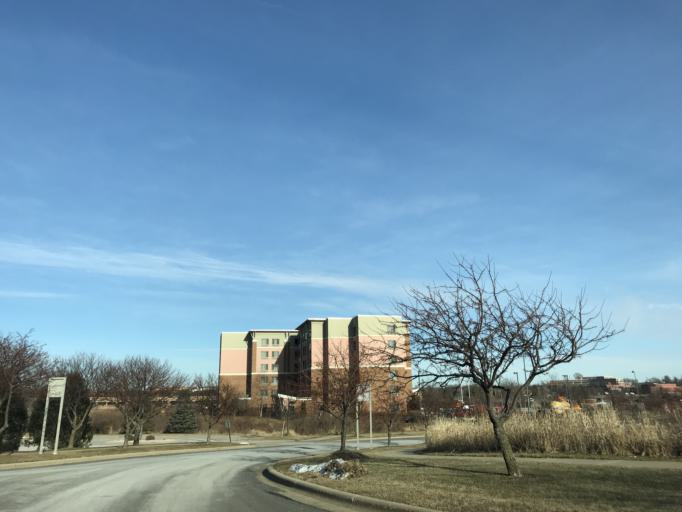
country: US
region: Wisconsin
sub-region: Dane County
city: Maple Bluff
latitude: 43.1432
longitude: -89.2977
